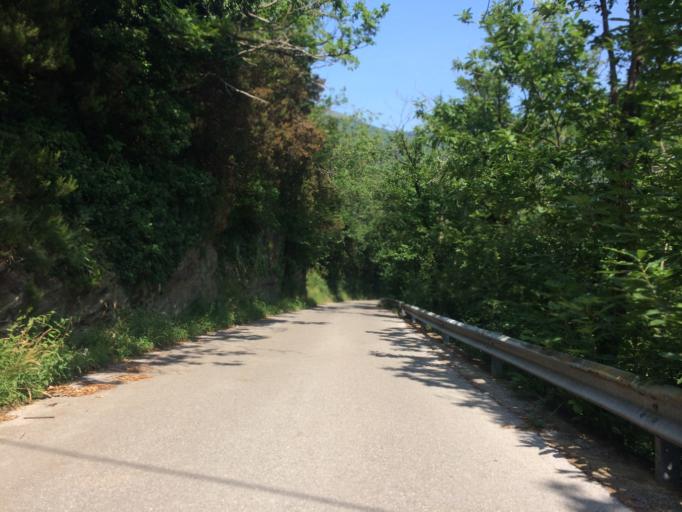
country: IT
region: Liguria
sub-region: Provincia di Genova
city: Sciarborasca
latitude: 44.3990
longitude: 8.5775
